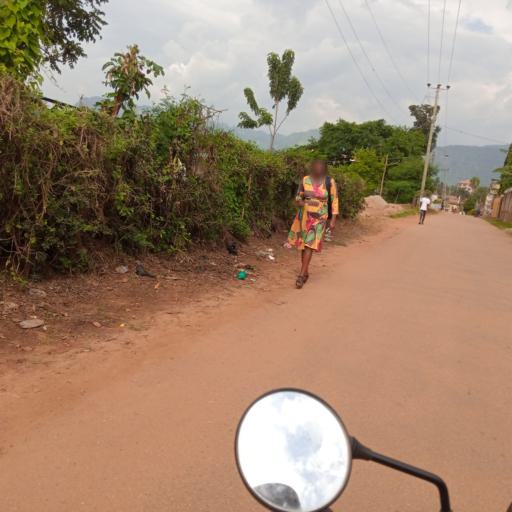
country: UG
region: Eastern Region
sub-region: Mbale District
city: Mbale
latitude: 1.0748
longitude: 34.1801
